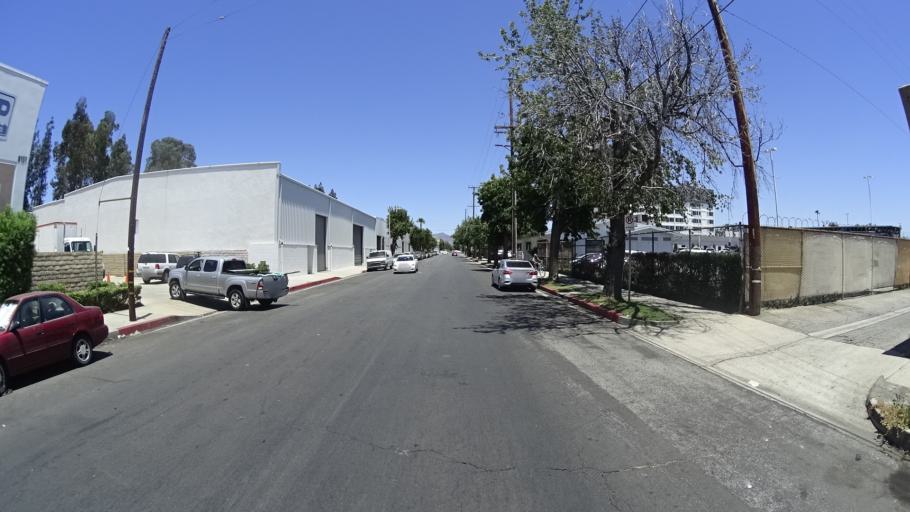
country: US
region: California
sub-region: Los Angeles County
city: Van Nuys
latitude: 34.2189
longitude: -118.4722
